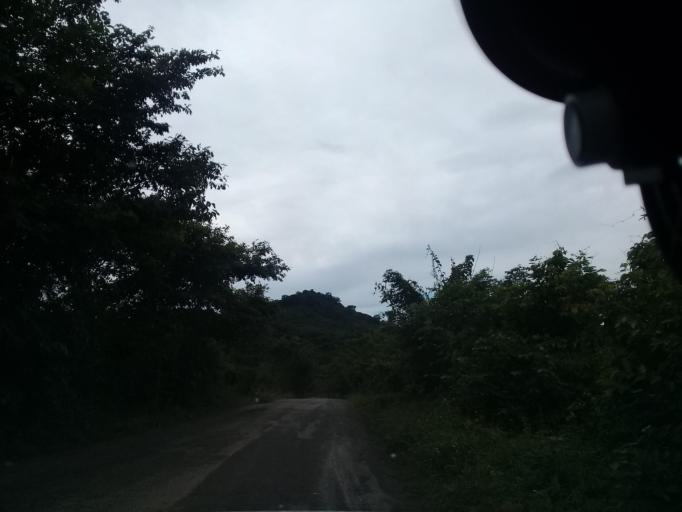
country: MX
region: Hidalgo
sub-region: Huejutla de Reyes
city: Chalahuiyapa
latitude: 21.2043
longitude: -98.3539
